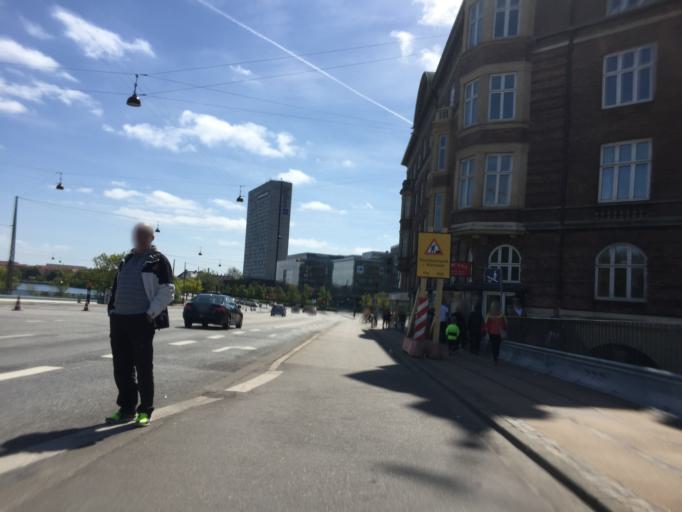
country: DK
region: Capital Region
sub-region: Kobenhavn
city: Christianshavn
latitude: 55.6694
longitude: 12.5802
